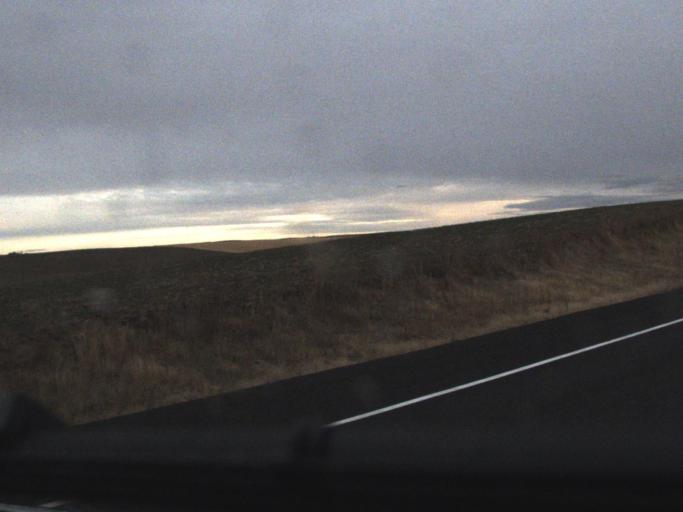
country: US
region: Washington
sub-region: Adams County
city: Ritzville
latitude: 46.7952
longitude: -118.4279
